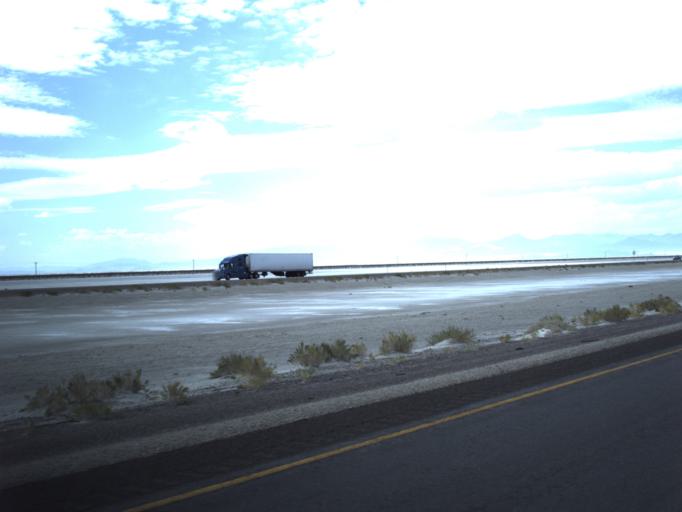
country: US
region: Utah
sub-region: Tooele County
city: Wendover
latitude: 40.7377
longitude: -113.7660
